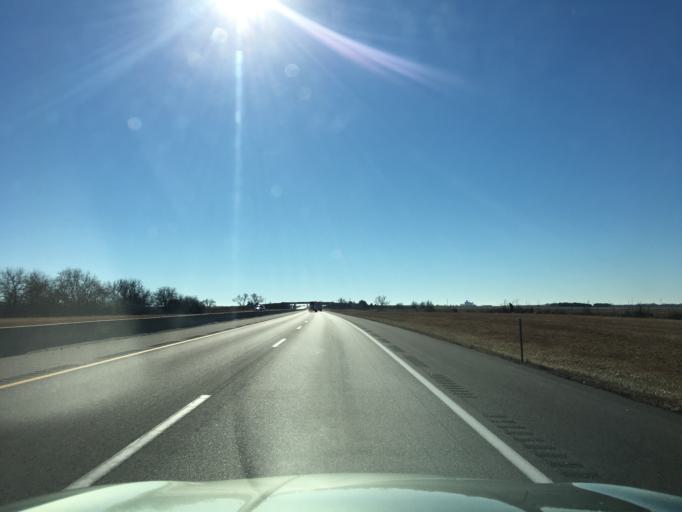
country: US
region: Kansas
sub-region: Sumner County
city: Wellington
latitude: 37.3104
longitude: -97.3406
